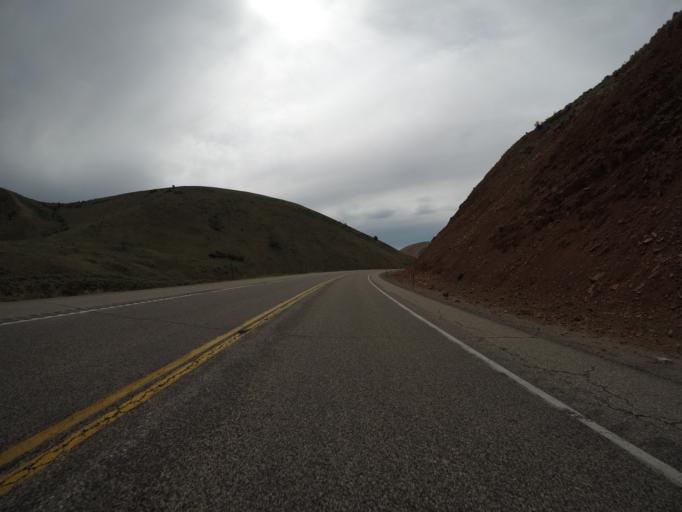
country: US
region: Wyoming
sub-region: Lincoln County
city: Kemmerer
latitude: 41.8227
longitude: -110.8349
